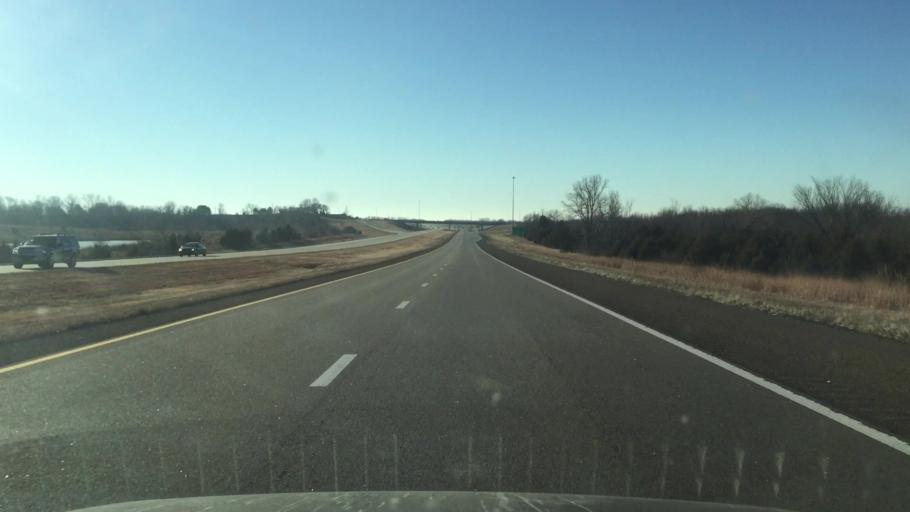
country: US
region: Kansas
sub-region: Miami County
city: Paola
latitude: 38.6285
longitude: -94.8361
